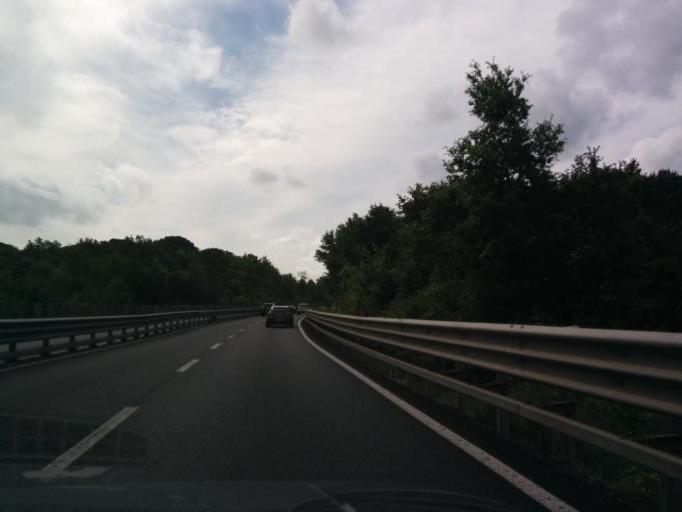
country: IT
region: Tuscany
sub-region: Province of Florence
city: Sambuca
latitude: 43.5416
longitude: 11.2187
